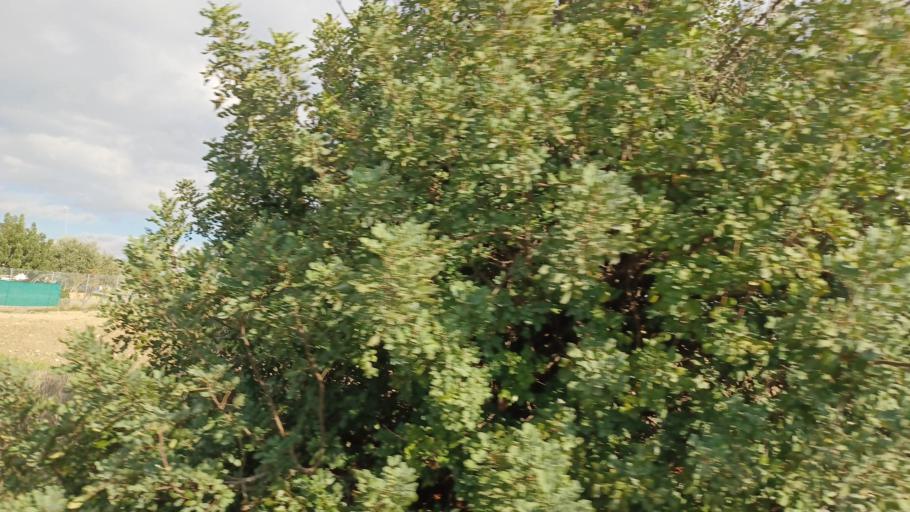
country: CY
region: Larnaka
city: Kofinou
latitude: 34.8128
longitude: 33.3481
